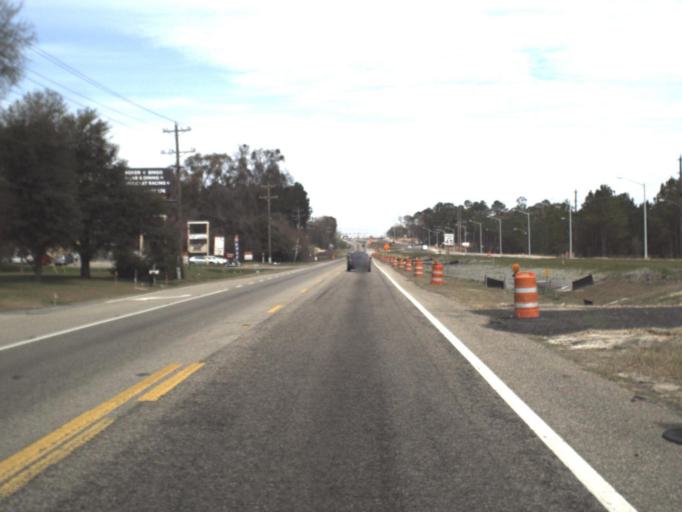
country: US
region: Florida
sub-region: Leon County
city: Tallahassee
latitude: 30.4255
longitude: -84.3528
